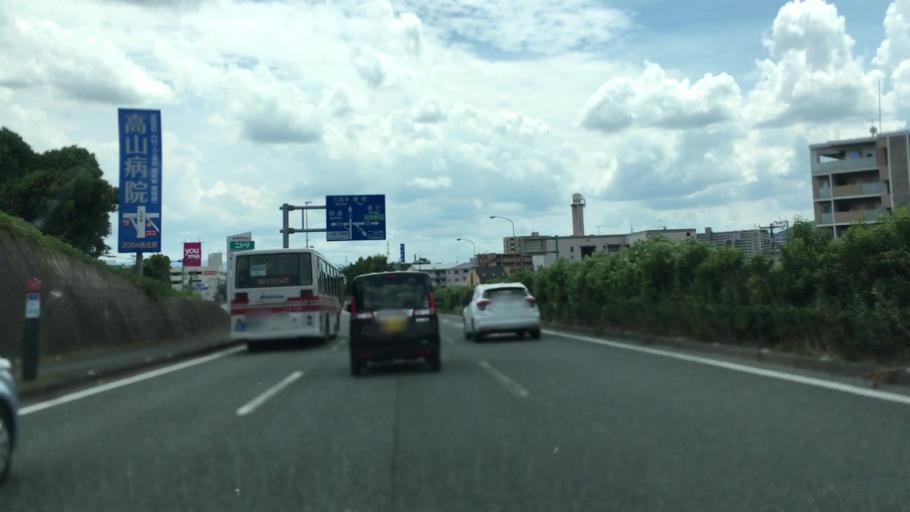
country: JP
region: Fukuoka
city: Chikushino-shi
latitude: 33.4882
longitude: 130.5358
